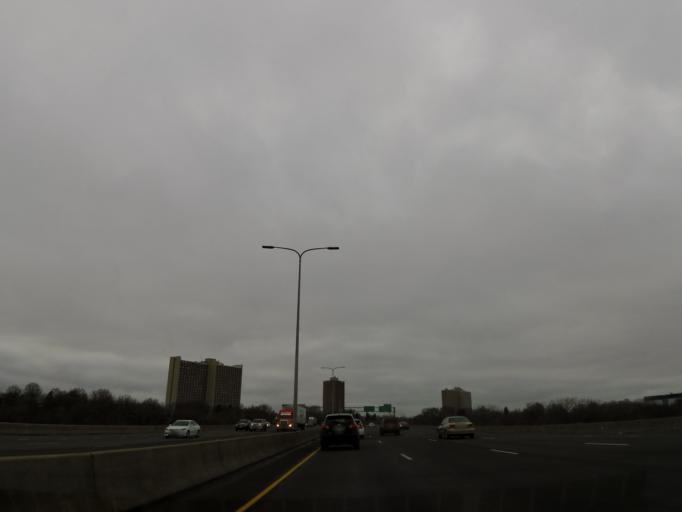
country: US
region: Minnesota
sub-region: Ramsey County
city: Lauderdale
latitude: 44.9660
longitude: -93.2245
